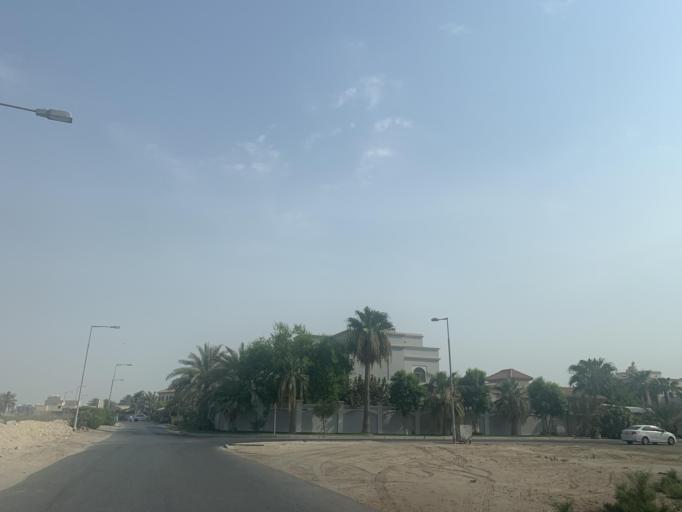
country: BH
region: Manama
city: Jidd Hafs
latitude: 26.2152
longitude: 50.4920
